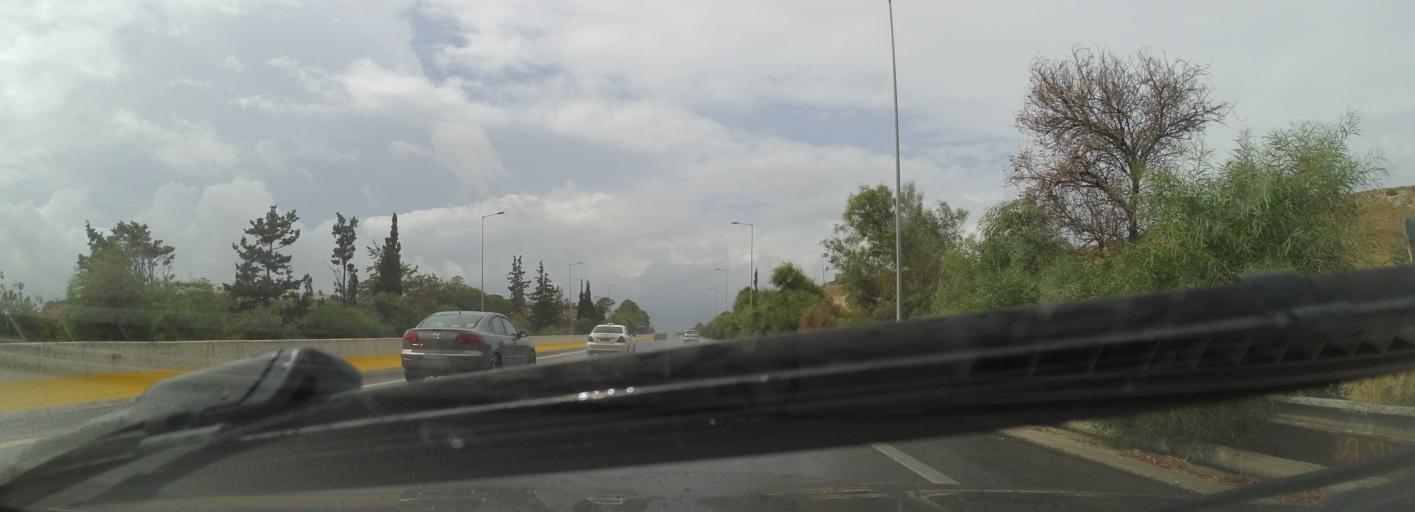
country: GR
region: Crete
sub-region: Nomos Irakleiou
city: Gazi
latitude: 35.3227
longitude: 25.0957
